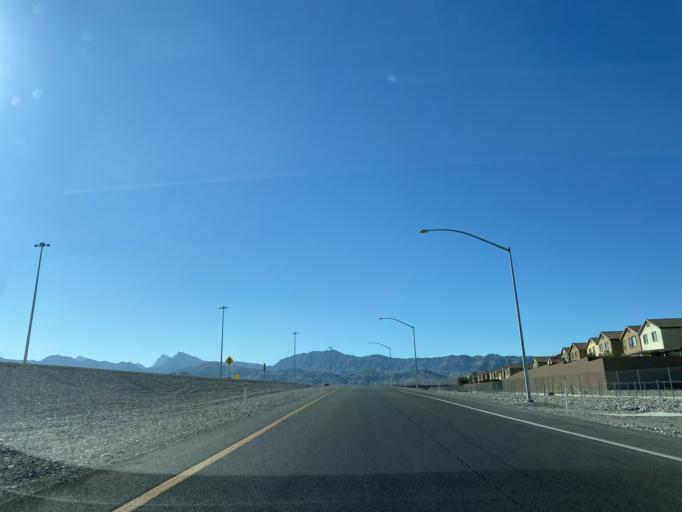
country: US
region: Nevada
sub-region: Clark County
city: Summerlin South
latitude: 36.2810
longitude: -115.2905
